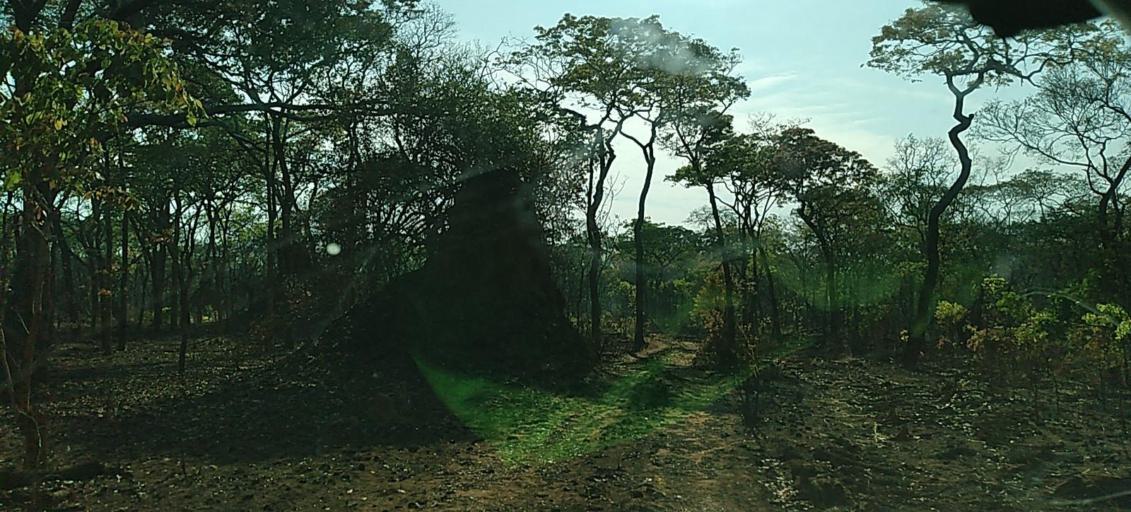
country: ZM
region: North-Western
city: Kalengwa
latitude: -13.2290
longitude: 25.0793
